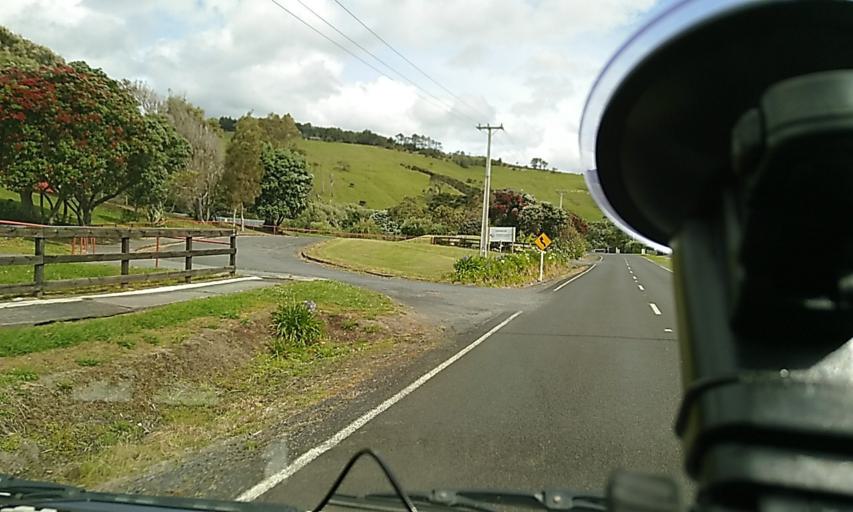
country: NZ
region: Northland
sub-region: Far North District
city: Ahipara
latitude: -35.5291
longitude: 173.3898
